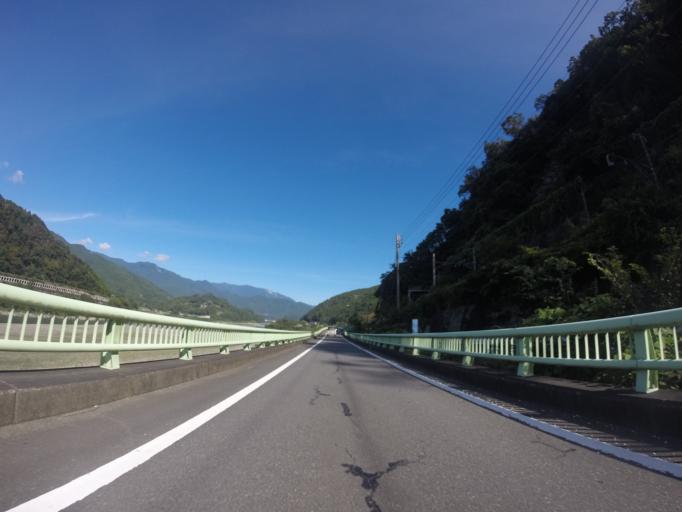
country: JP
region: Shizuoka
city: Fujinomiya
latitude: 35.2576
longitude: 138.4804
